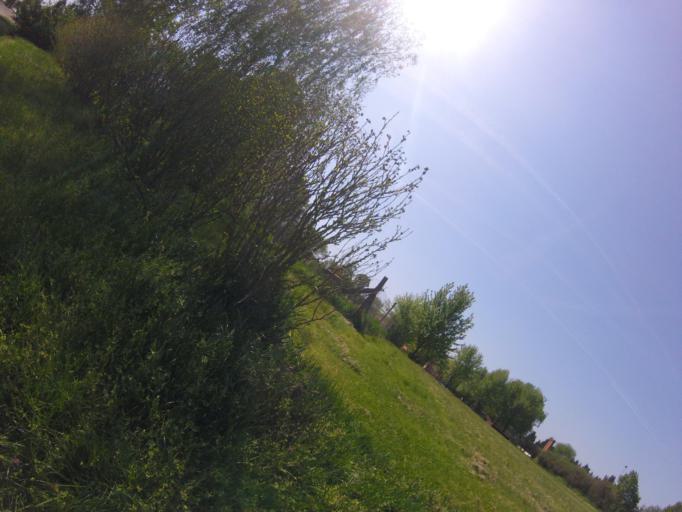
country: HU
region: Pest
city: Danszentmiklos
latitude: 47.1701
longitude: 19.5056
